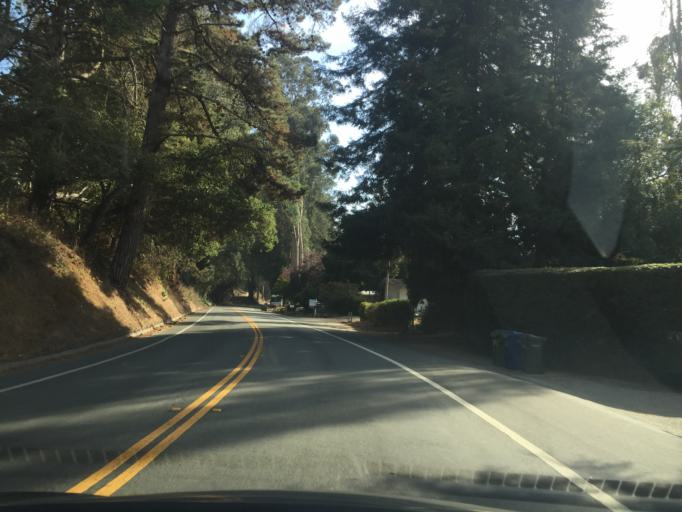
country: US
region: California
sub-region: Santa Cruz County
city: La Selva Beach
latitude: 36.9368
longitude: -121.8596
